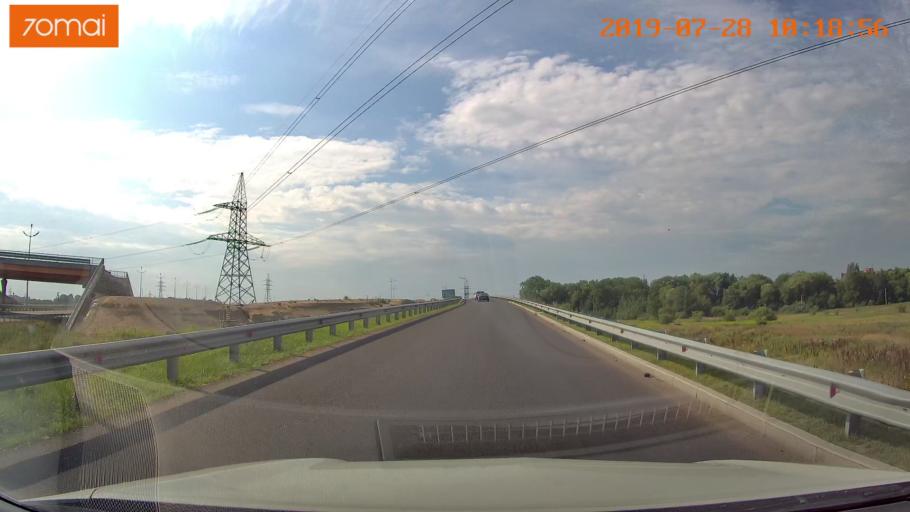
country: RU
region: Kaliningrad
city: Maloye Isakovo
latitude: 54.7522
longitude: 20.5864
